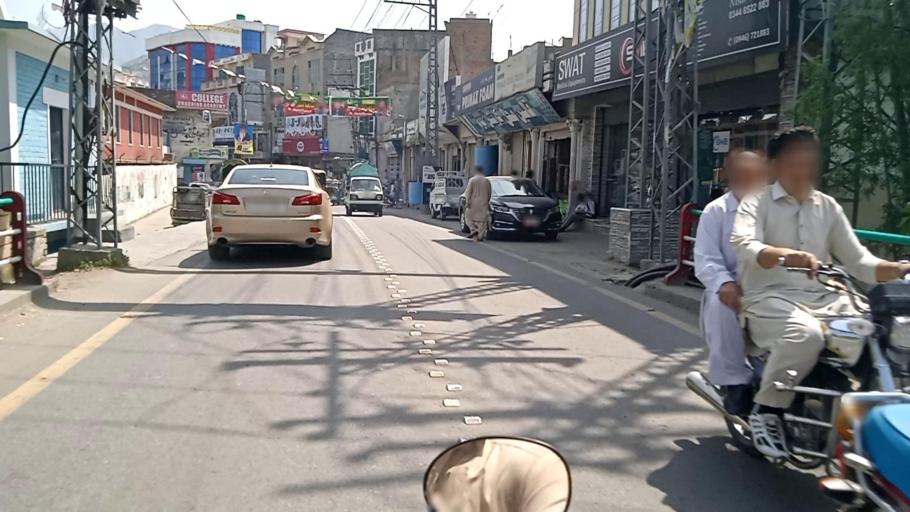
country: PK
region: Khyber Pakhtunkhwa
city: Mingora
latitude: 34.7705
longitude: 72.3585
